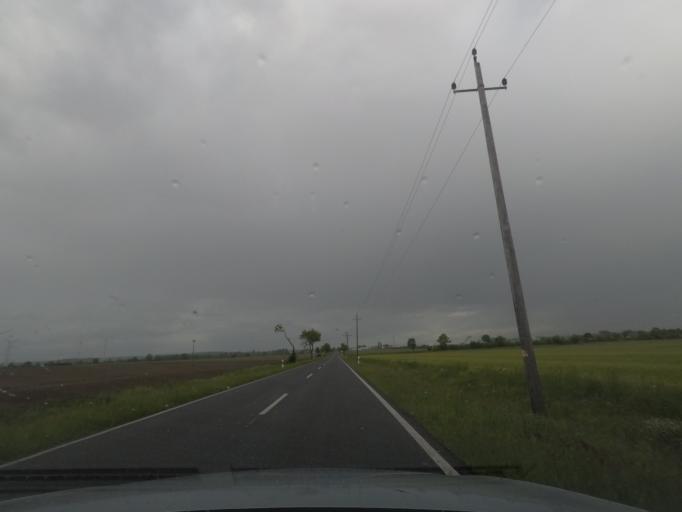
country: DE
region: Saxony-Anhalt
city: Kusey
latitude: 52.5685
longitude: 11.0825
